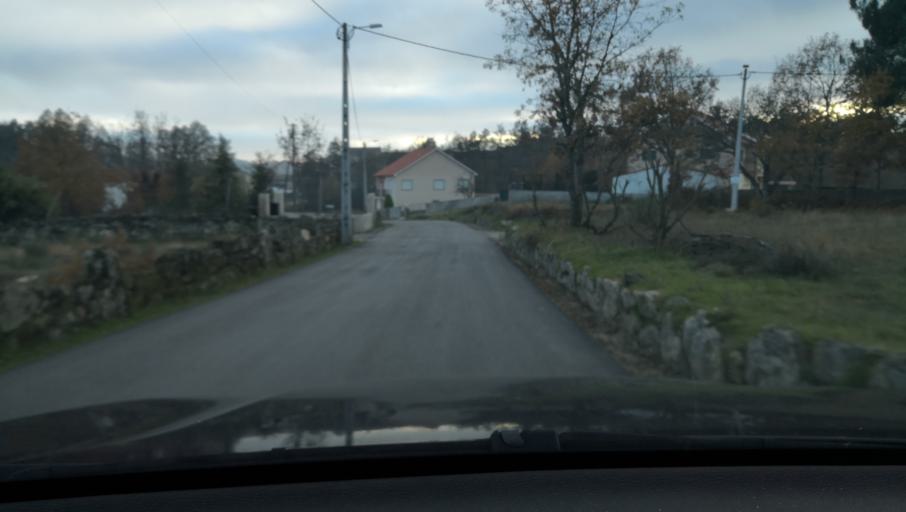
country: PT
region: Vila Real
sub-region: Vila Real
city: Vila Real
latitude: 41.3423
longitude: -7.6626
